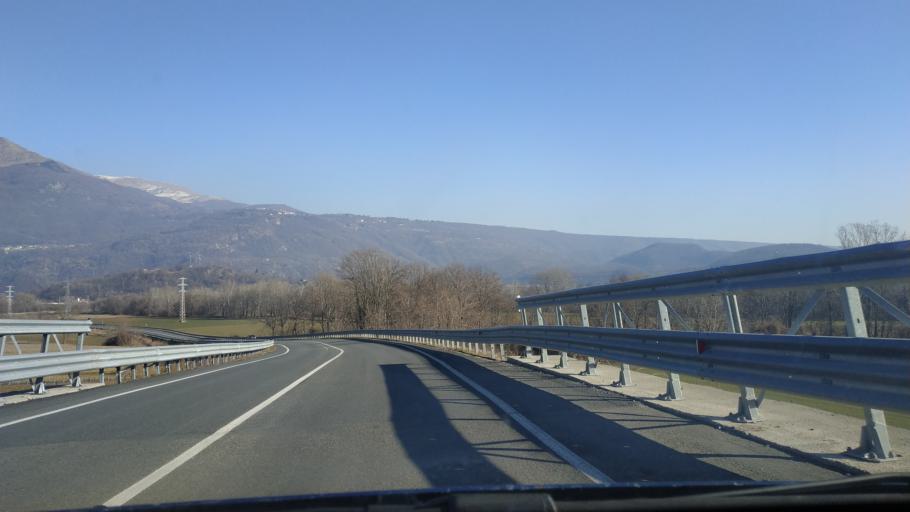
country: IT
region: Piedmont
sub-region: Provincia di Torino
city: Quassolo
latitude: 45.5009
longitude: 7.8324
